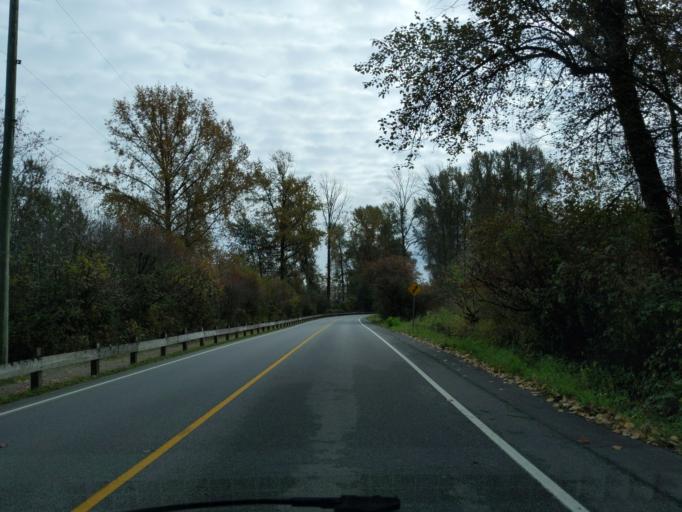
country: CA
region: British Columbia
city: Maple Ridge
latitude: 49.2012
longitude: -122.5962
